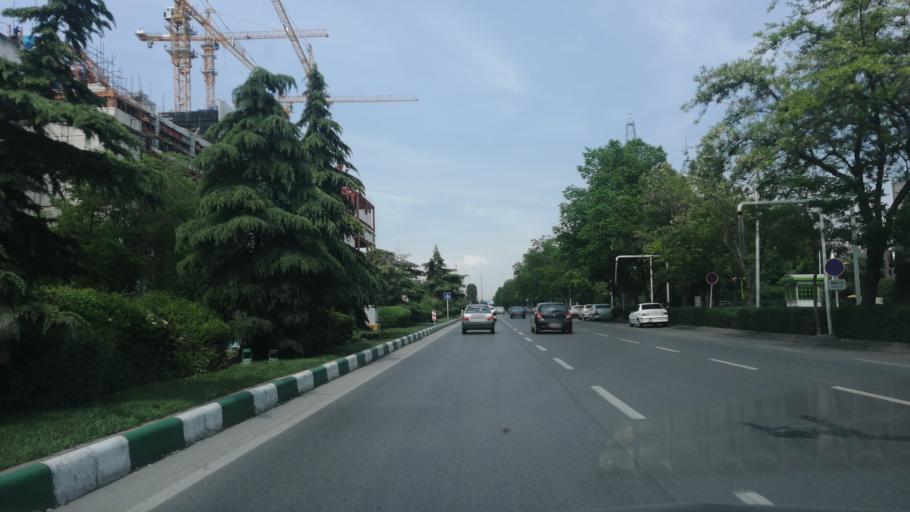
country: IR
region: Razavi Khorasan
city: Mashhad
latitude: 36.3160
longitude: 59.5615
